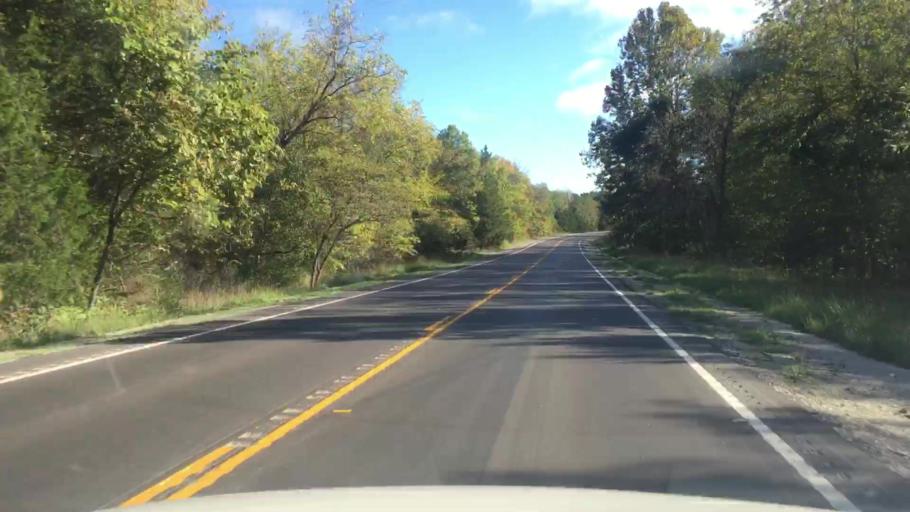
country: US
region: Missouri
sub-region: Howard County
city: New Franklin
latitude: 38.9876
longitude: -92.5361
